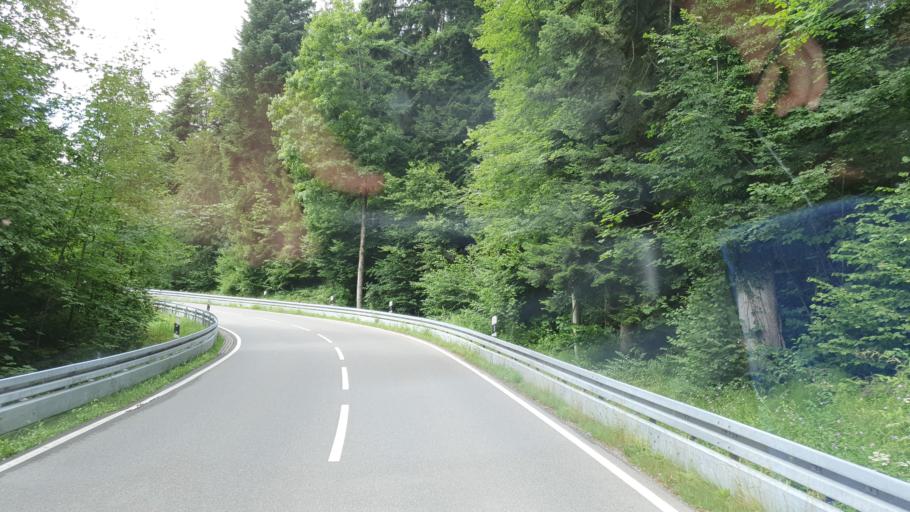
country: DE
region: Bavaria
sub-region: Swabia
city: Scheidegg
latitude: 47.5944
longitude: 9.8370
